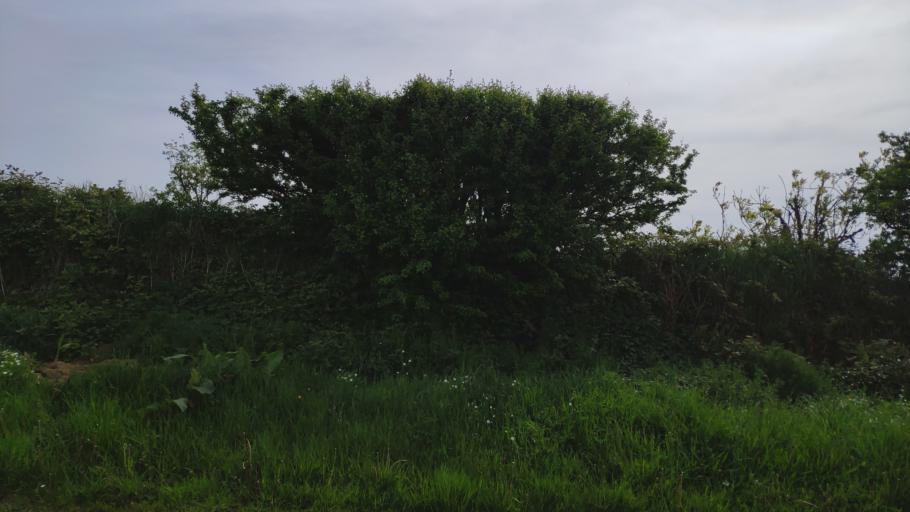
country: IE
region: Munster
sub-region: County Cork
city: Blarney
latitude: 51.9692
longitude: -8.5135
